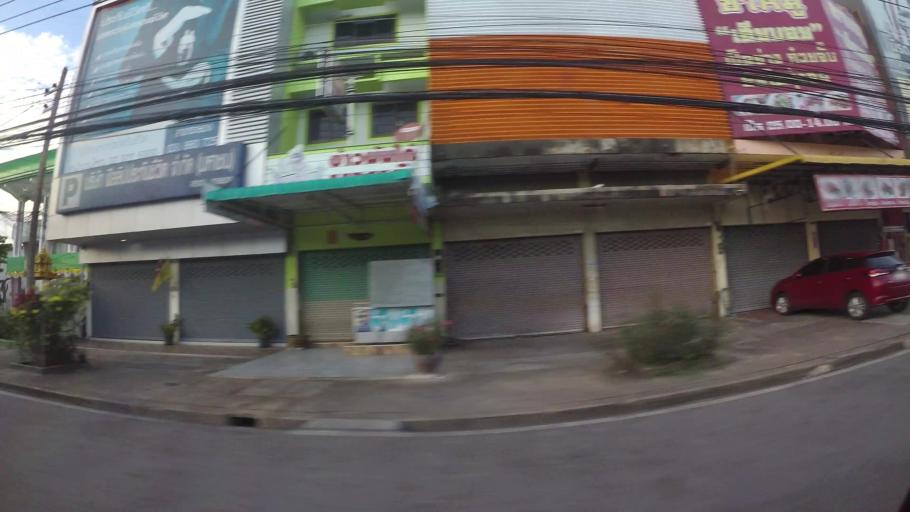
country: TH
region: Rayong
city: Rayong
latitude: 12.6796
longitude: 101.2856
